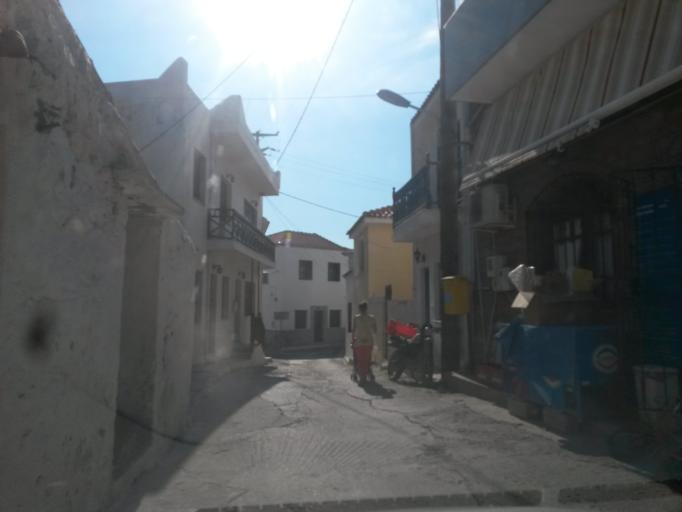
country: GR
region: North Aegean
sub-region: Nomos Lesvou
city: Eresos
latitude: 39.2111
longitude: 25.8520
